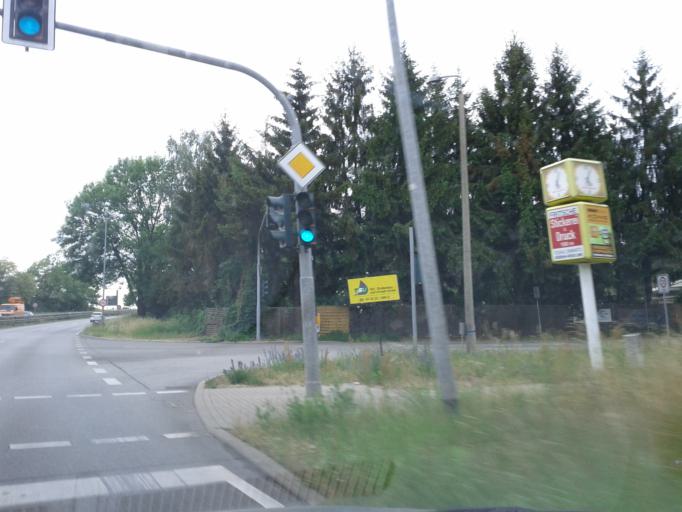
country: DE
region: Brandenburg
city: Hoppegarten
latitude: 52.4991
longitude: 13.6468
